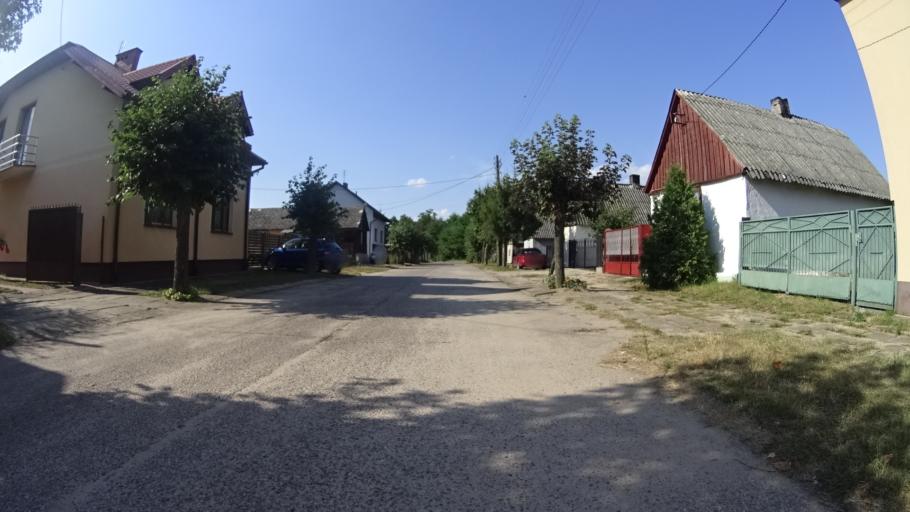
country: PL
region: Masovian Voivodeship
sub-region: Powiat bialobrzeski
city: Wysmierzyce
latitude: 51.6277
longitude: 20.8193
